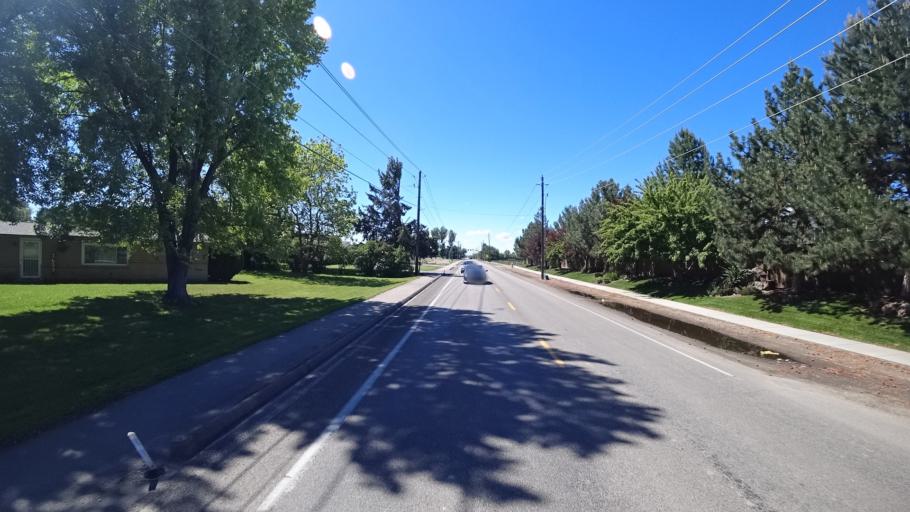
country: US
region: Idaho
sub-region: Ada County
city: Meridian
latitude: 43.6437
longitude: -116.3745
